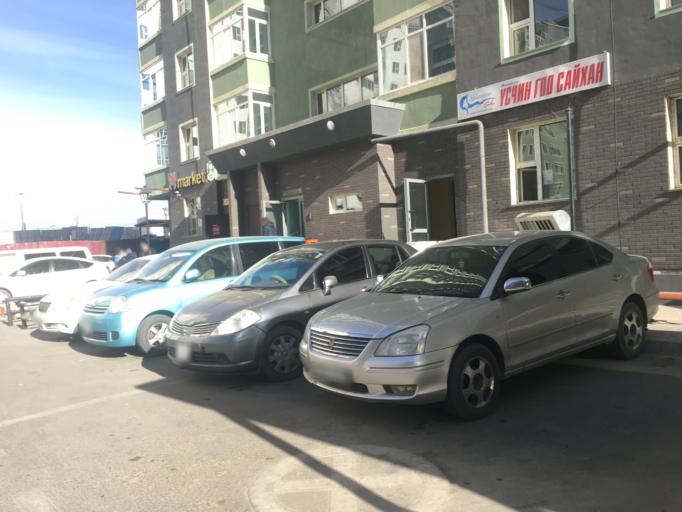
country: MN
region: Ulaanbaatar
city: Ulaanbaatar
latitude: 47.9208
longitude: 106.8196
